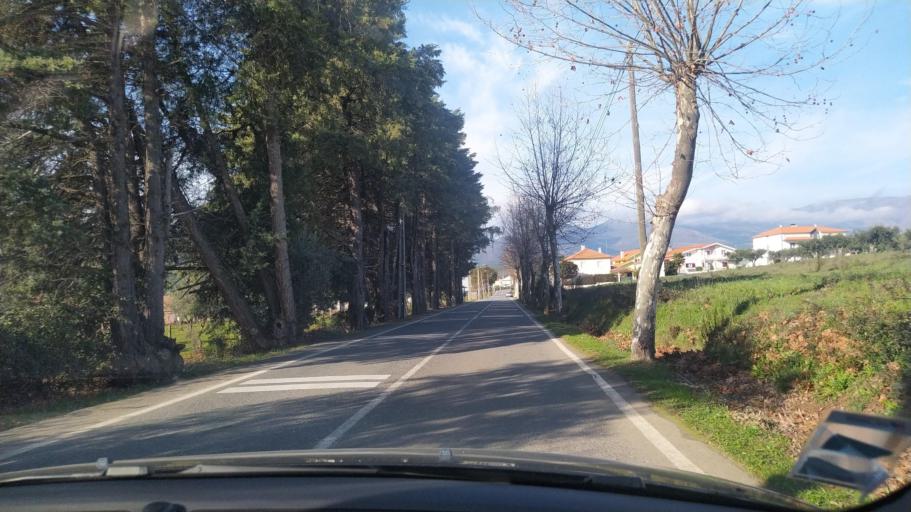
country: PT
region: Castelo Branco
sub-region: Concelho do Fundao
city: Aldeia de Joanes
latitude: 40.1920
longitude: -7.6380
